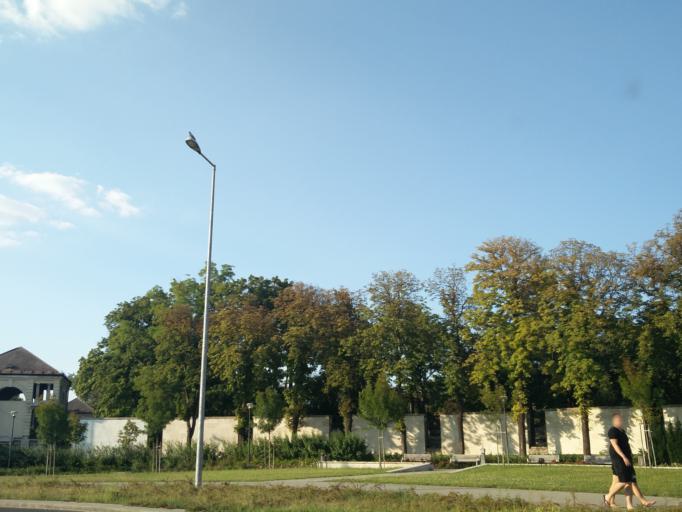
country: HU
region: Budapest
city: Budapest X. keruelet
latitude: 47.4730
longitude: 19.1785
